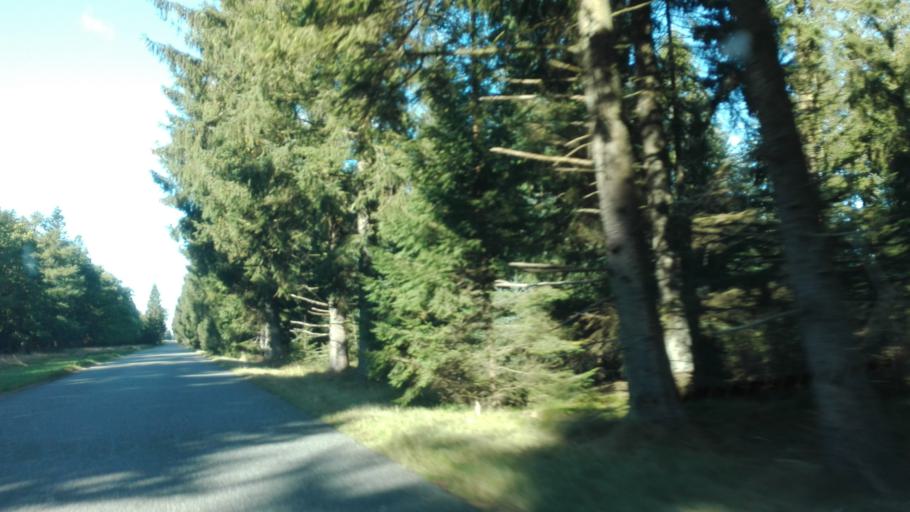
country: DK
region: Central Jutland
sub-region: Ikast-Brande Kommune
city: Bording Kirkeby
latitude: 56.0726
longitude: 9.3717
